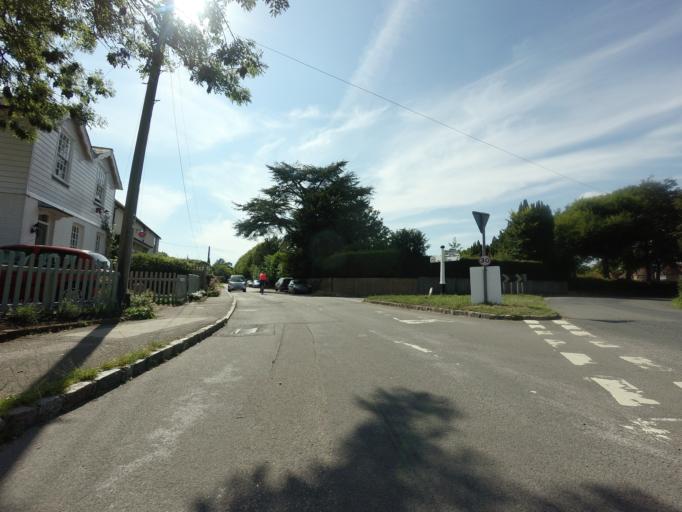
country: GB
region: England
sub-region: East Sussex
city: Rye
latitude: 50.9822
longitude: 0.7305
